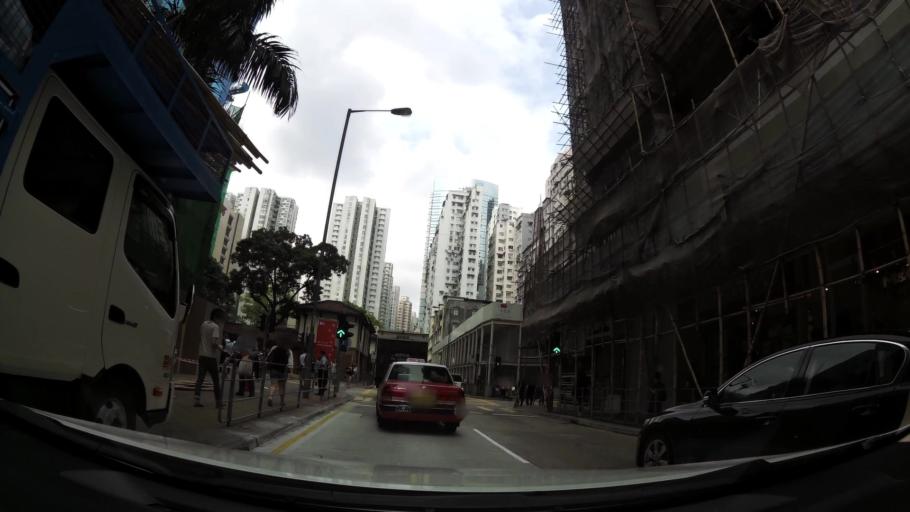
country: HK
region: Wanchai
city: Wan Chai
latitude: 22.2883
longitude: 114.1924
